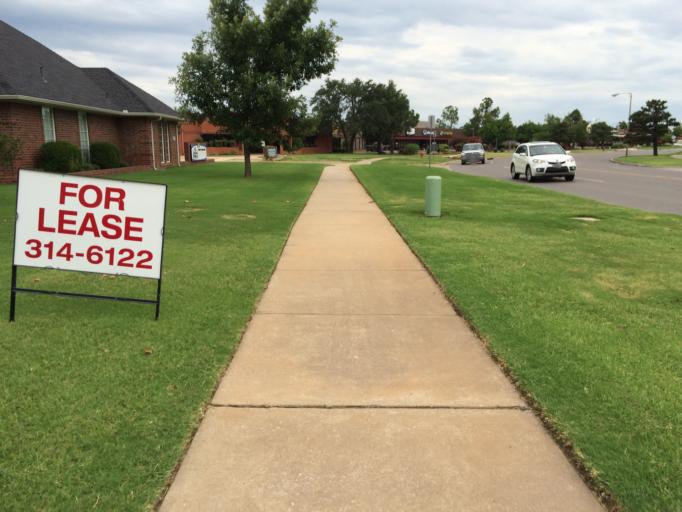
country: US
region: Oklahoma
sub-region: Cleveland County
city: Norman
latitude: 35.2287
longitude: -97.4800
